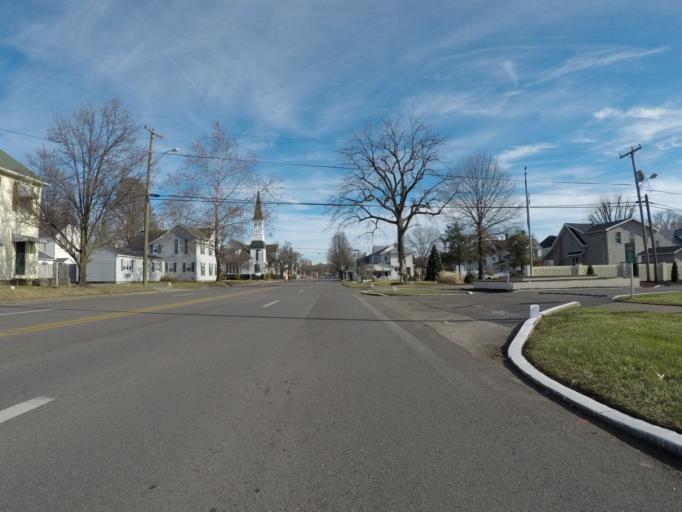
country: US
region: West Virginia
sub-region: Wayne County
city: Ceredo
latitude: 38.3967
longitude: -82.5605
